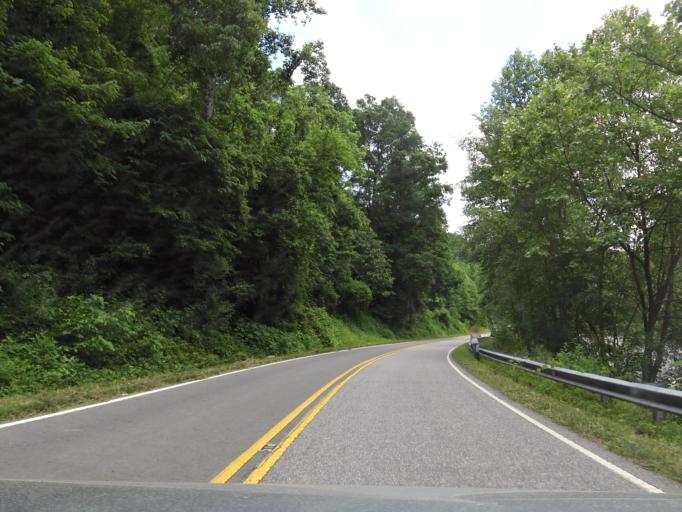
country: US
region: North Carolina
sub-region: Graham County
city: Robbinsville
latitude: 35.4386
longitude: -83.9208
